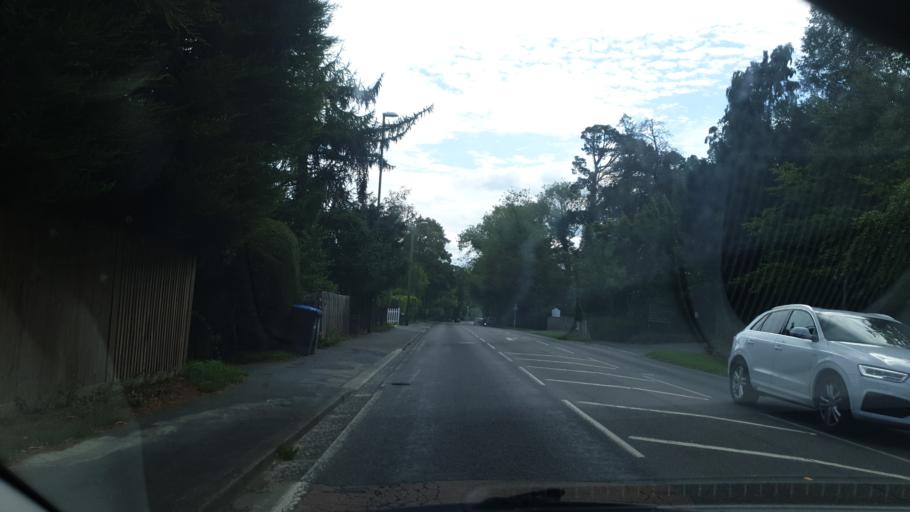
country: GB
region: England
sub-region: West Sussex
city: East Grinstead
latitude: 51.1149
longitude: 0.0165
